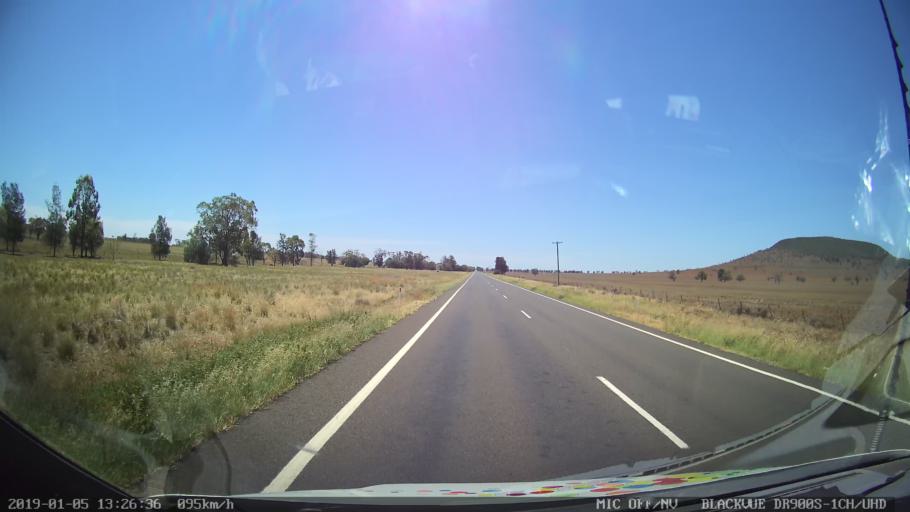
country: AU
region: New South Wales
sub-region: Gunnedah
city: Gunnedah
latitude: -31.0516
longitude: 150.0179
